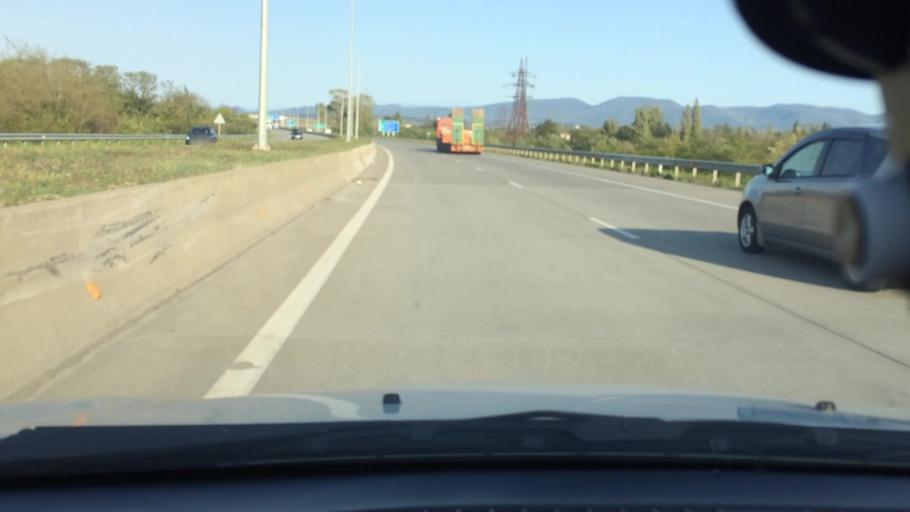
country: GE
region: Imereti
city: Zestap'oni
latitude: 42.1532
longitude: 42.9585
